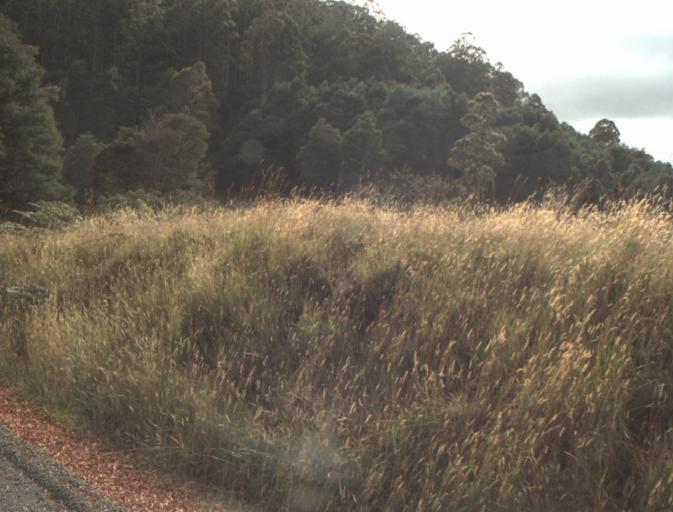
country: AU
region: Tasmania
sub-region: Dorset
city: Scottsdale
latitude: -41.4458
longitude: 147.5871
